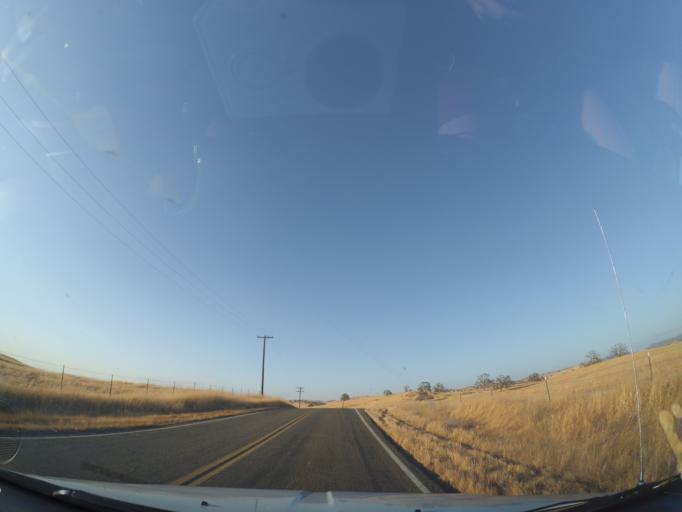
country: US
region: California
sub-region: Merced County
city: Planada
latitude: 37.5130
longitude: -120.3165
